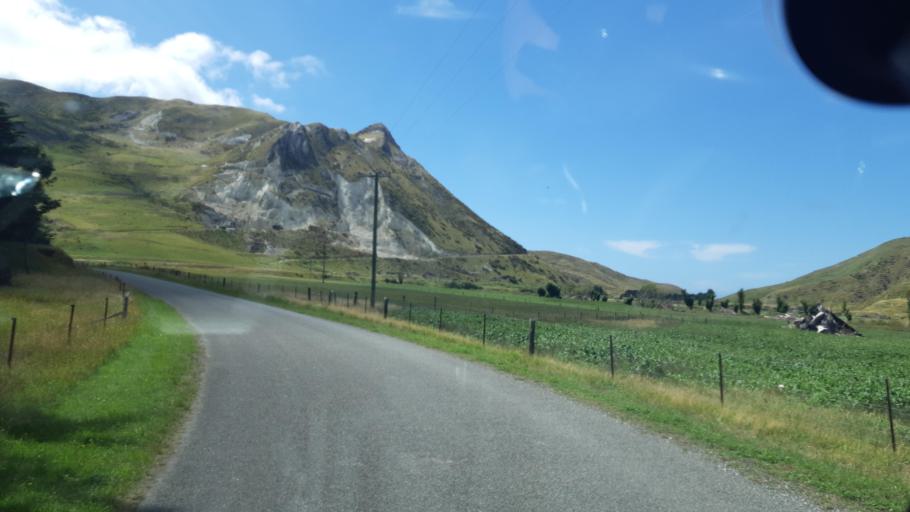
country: NZ
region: Marlborough
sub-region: Marlborough District
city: Blenheim
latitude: -41.8315
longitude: 174.1701
